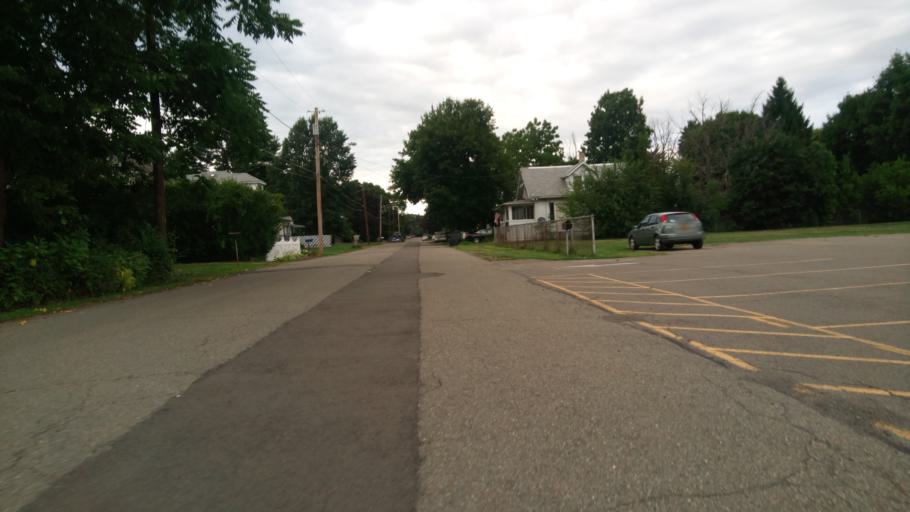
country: US
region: New York
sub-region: Chemung County
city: Southport
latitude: 42.0599
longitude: -76.8129
